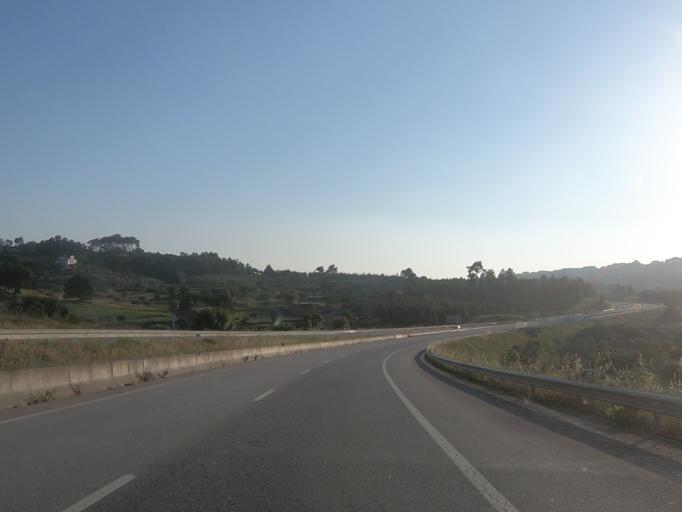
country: PT
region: Guarda
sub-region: Celorico da Beira
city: Celorico da Beira
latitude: 40.6271
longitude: -7.3784
